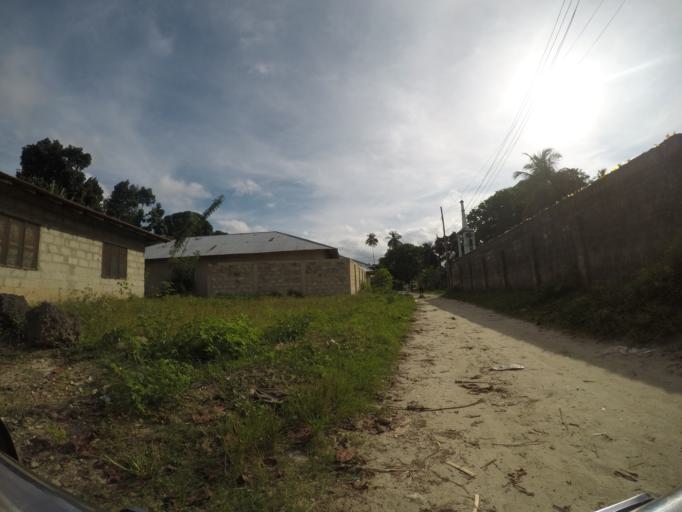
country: TZ
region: Pemba South
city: Chake Chake
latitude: -5.2240
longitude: 39.7785
